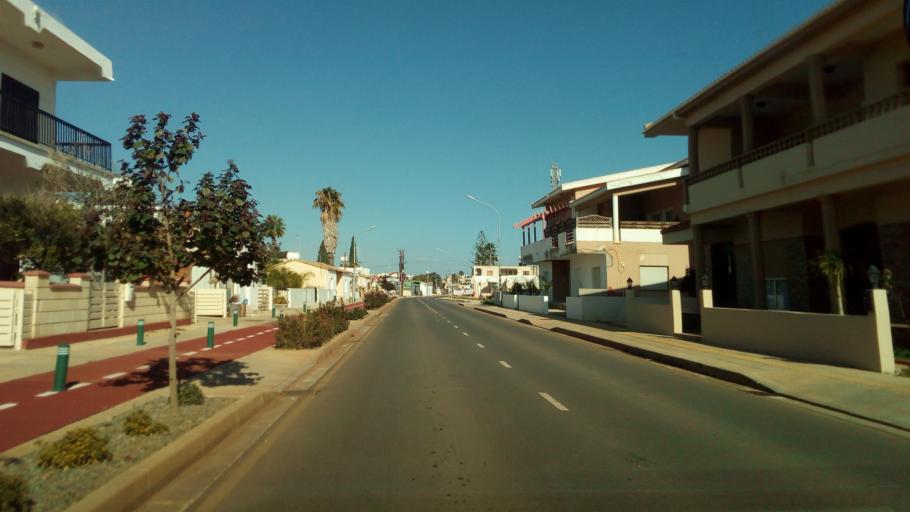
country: CY
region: Ammochostos
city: Avgorou
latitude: 35.0310
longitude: 33.8394
